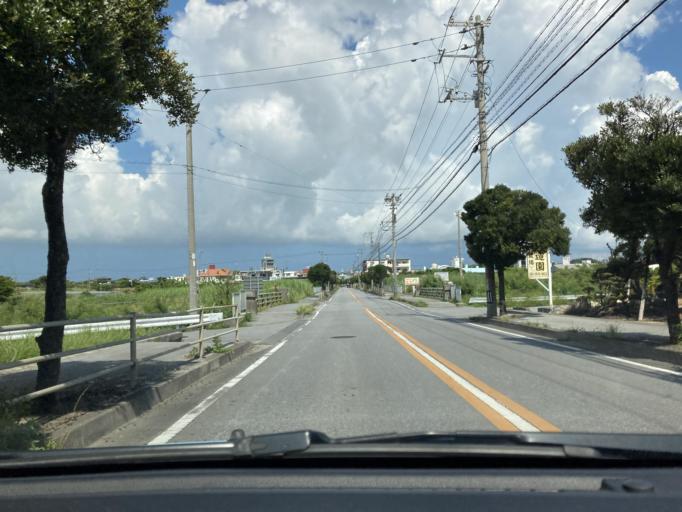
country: JP
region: Okinawa
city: Tomigusuku
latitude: 26.1547
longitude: 127.7500
